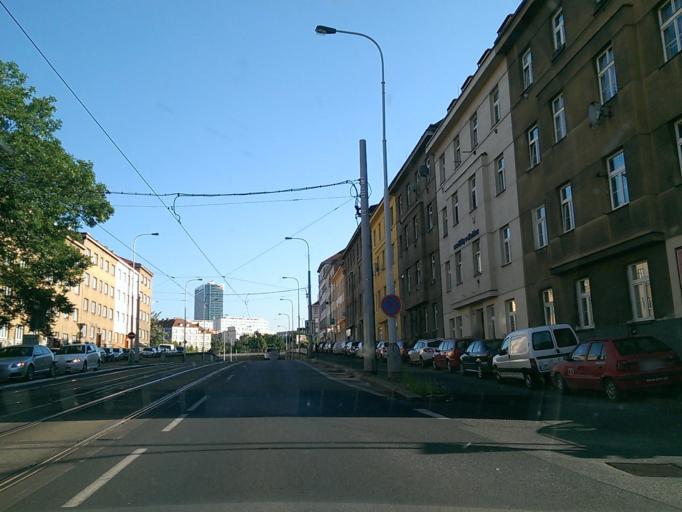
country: CZ
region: Praha
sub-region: Praha 2
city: Vysehrad
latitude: 50.0598
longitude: 14.4360
